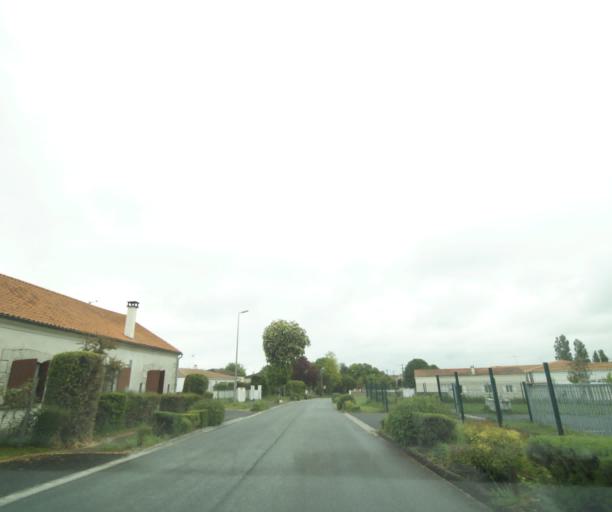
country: FR
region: Poitou-Charentes
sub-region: Departement de la Charente-Maritime
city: Perignac
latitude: 45.6488
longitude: -0.5093
